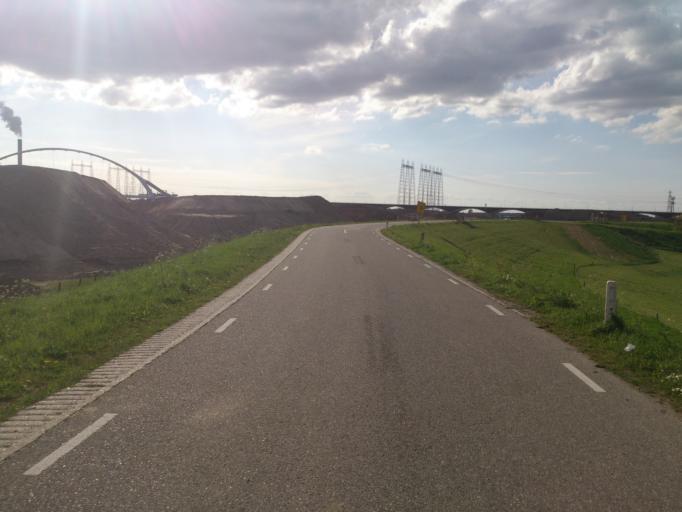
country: NL
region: Gelderland
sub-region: Gemeente Nijmegen
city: Nijmegen
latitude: 51.8596
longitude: 5.8542
